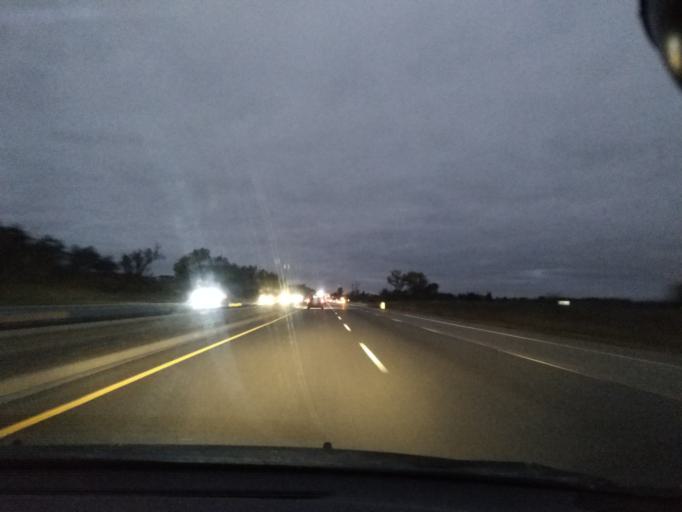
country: CA
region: Ontario
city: Bradford West Gwillimbury
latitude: 44.1125
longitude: -79.6340
